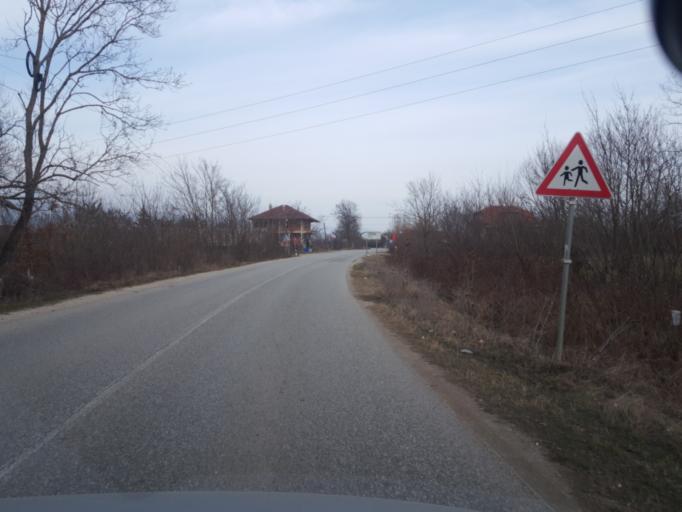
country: XK
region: Pec
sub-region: Komuna e Istogut
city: Istok
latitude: 42.7381
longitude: 20.4791
